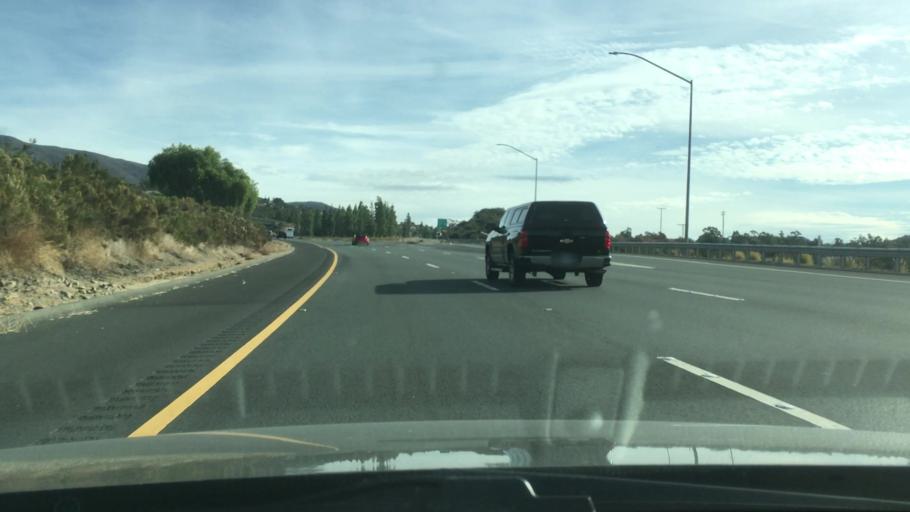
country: US
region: California
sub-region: San Diego County
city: Alpine
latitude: 32.8392
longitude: -116.7846
